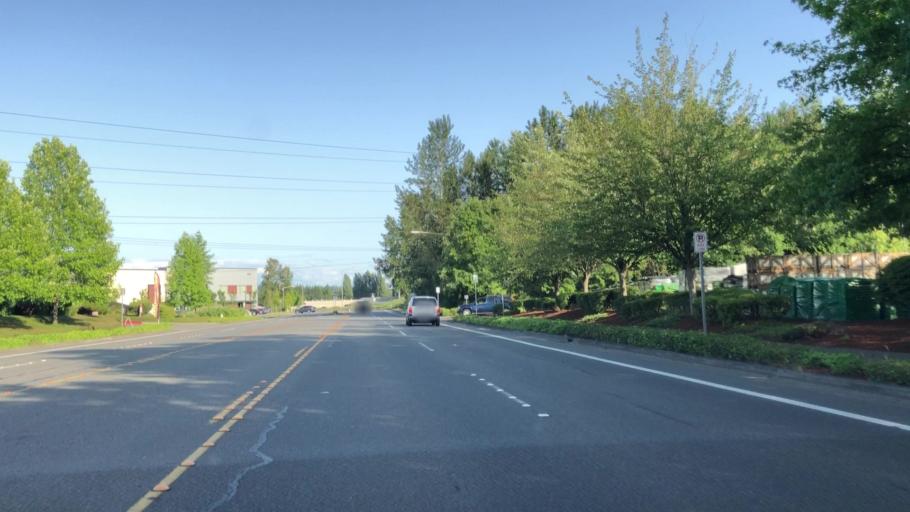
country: US
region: Washington
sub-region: King County
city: Woodinville
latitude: 47.7601
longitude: -122.1761
